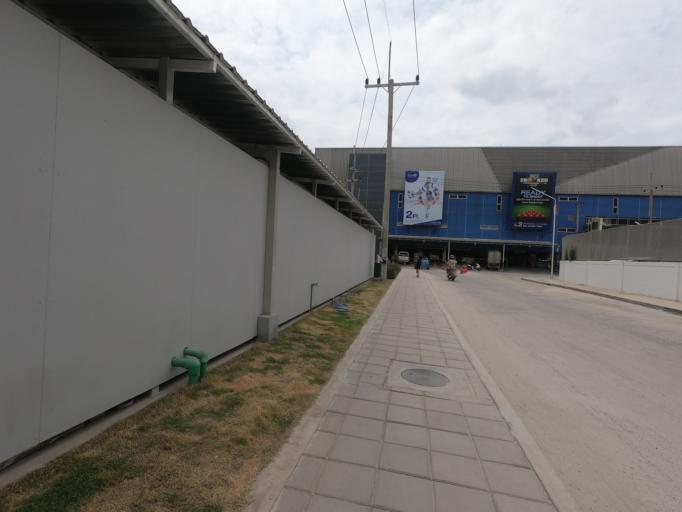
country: TH
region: Bangkok
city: Sai Mai
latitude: 13.9494
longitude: 100.6524
